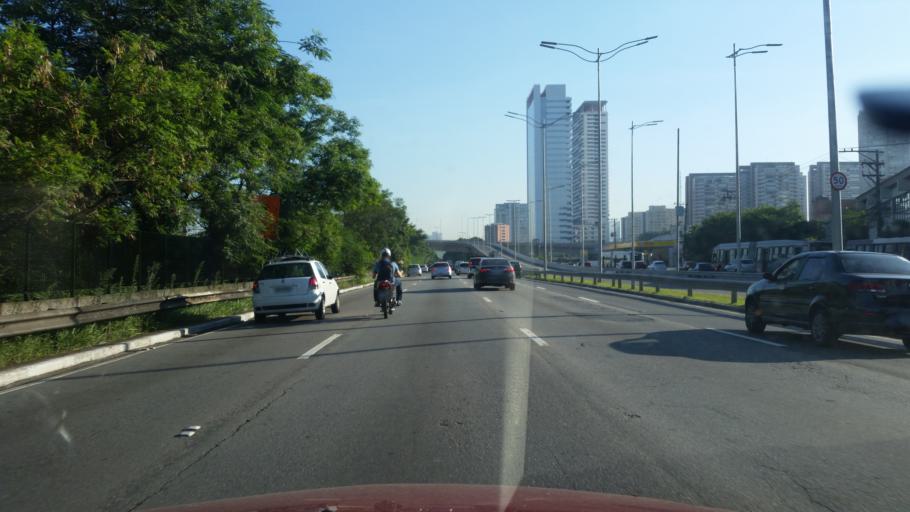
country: BR
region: Sao Paulo
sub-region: Taboao Da Serra
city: Taboao da Serra
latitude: -23.6367
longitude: -46.7203
